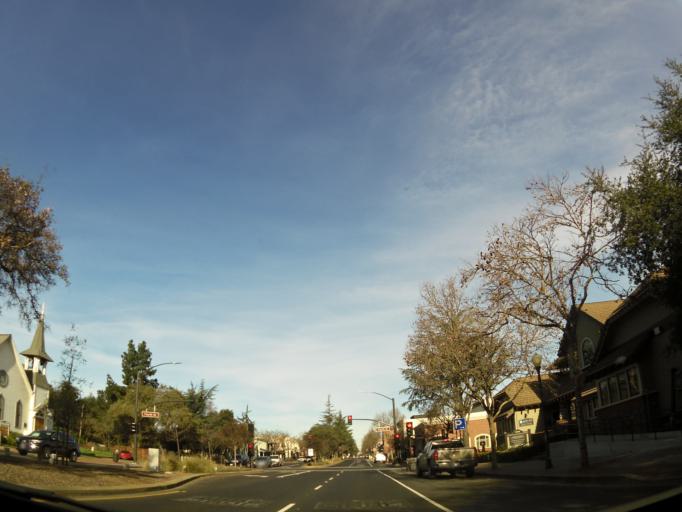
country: US
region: California
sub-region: Santa Clara County
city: Morgan Hill
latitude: 37.1268
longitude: -121.6513
